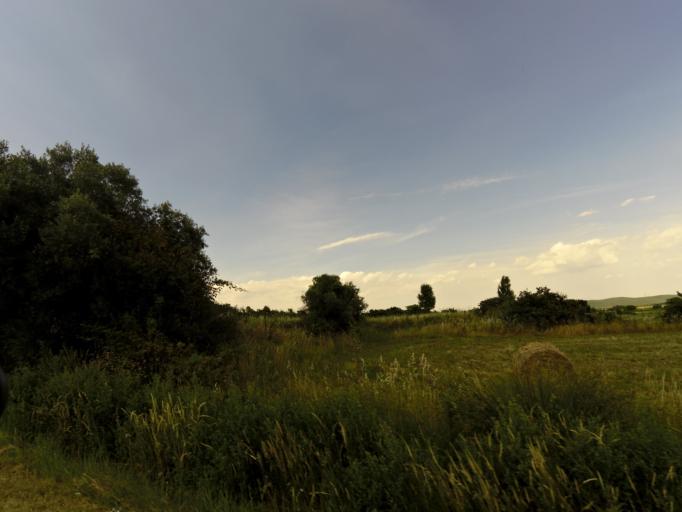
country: FR
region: Languedoc-Roussillon
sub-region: Departement du Gard
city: Sommieres
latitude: 43.8391
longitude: 4.0301
